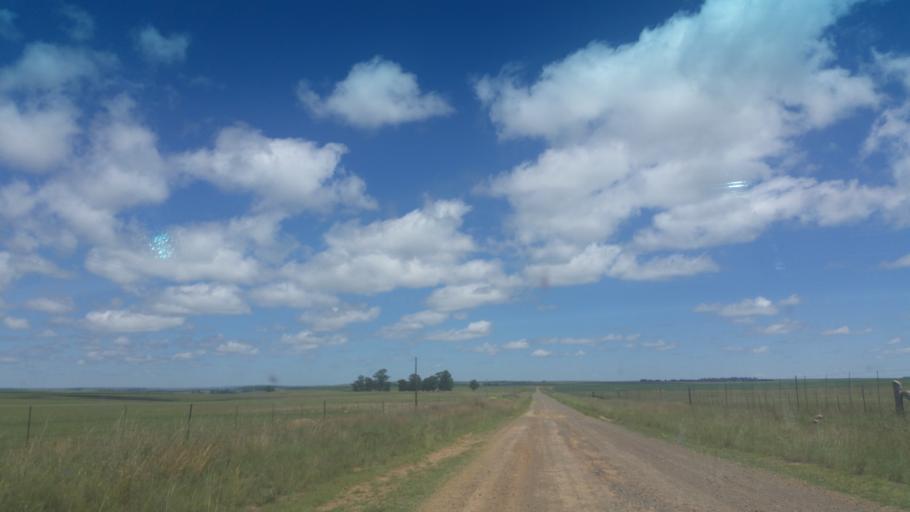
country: ZA
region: Orange Free State
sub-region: Thabo Mofutsanyana District Municipality
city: Harrismith
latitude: -28.1803
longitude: 29.0218
